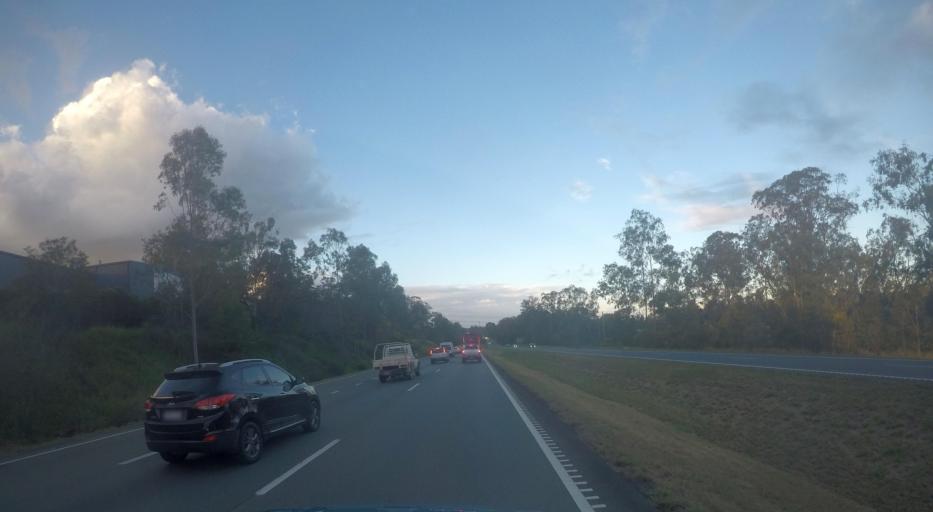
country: AU
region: Queensland
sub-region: Ipswich
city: Tivoli
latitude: -27.5796
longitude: 152.7710
